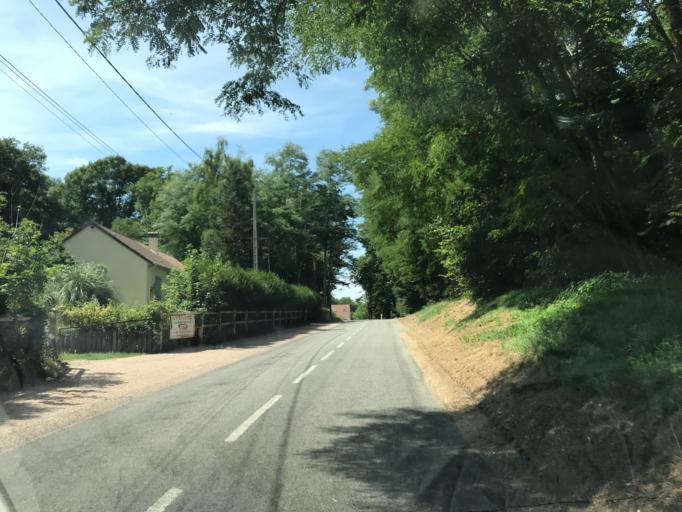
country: FR
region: Haute-Normandie
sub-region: Departement de l'Eure
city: Gasny
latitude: 49.0787
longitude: 1.5993
